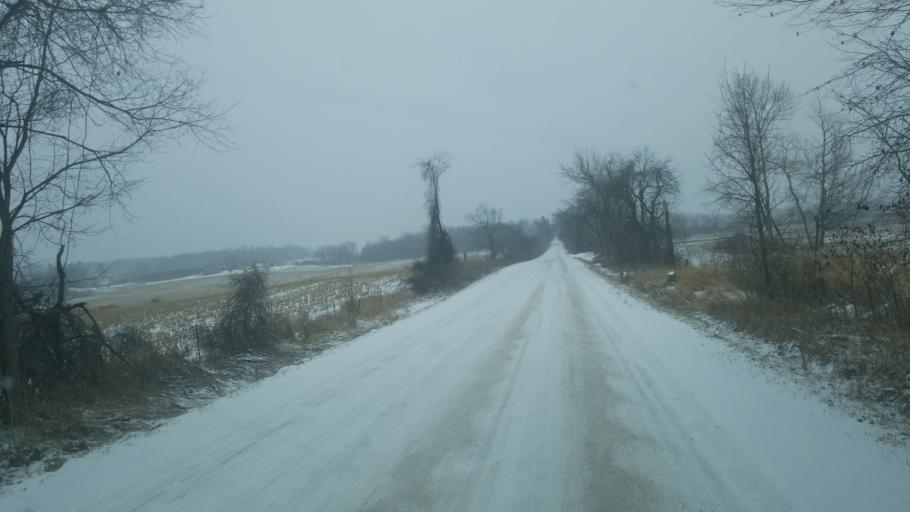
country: US
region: Michigan
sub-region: Osceola County
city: Reed City
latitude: 43.8498
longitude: -85.3940
